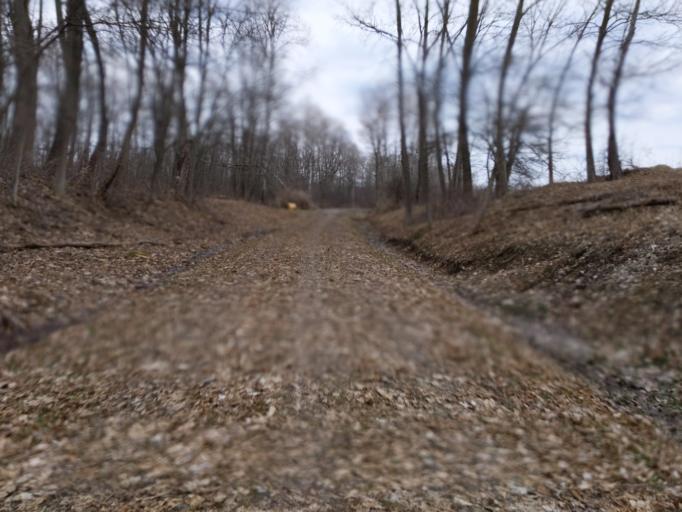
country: US
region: New York
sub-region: Tompkins County
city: Dryden
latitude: 42.5044
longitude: -76.3409
